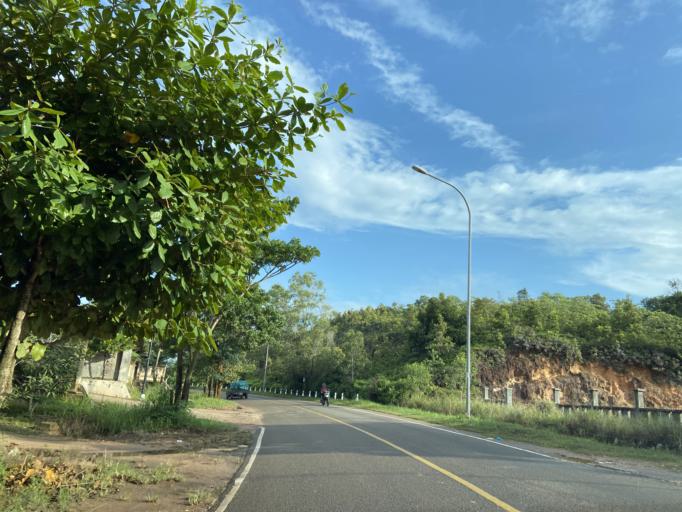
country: SG
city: Singapore
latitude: 0.9755
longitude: 104.0538
